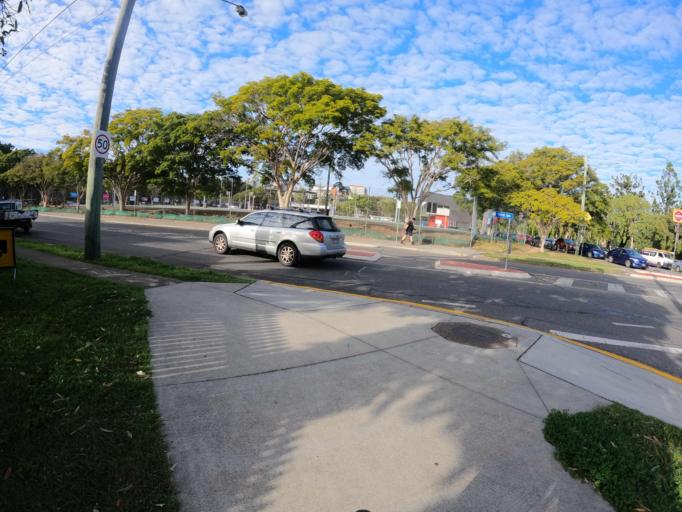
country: AU
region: Queensland
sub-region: Brisbane
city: Windsor
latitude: -27.4419
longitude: 153.0263
